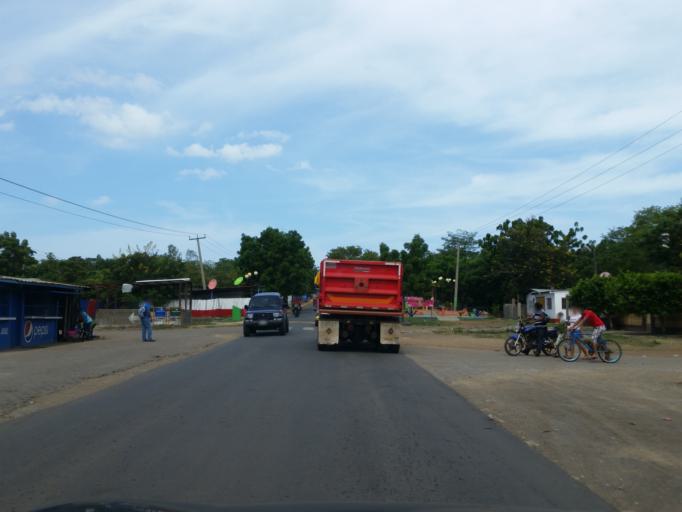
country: NI
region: Managua
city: Masachapa
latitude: 11.8131
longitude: -86.4858
